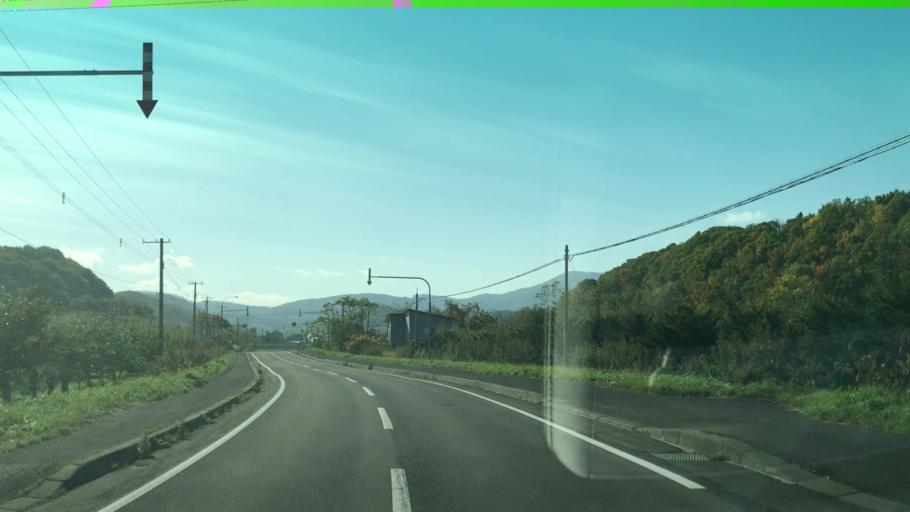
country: JP
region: Hokkaido
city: Yoichi
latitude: 43.1743
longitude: 140.8216
